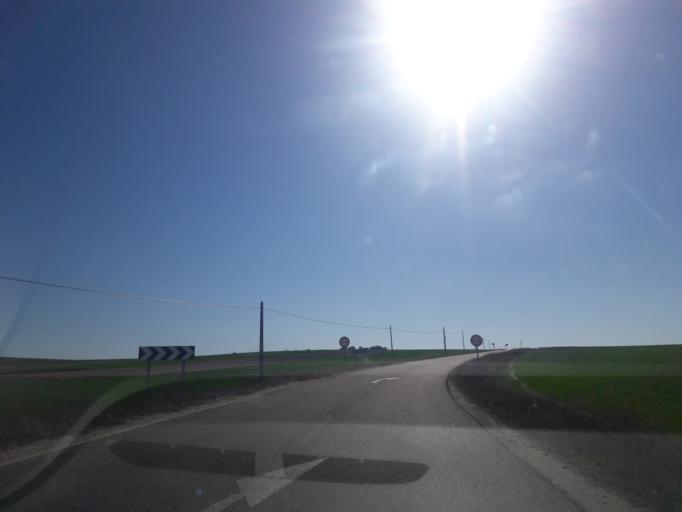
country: ES
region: Castille and Leon
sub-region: Provincia de Salamanca
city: Tordillos
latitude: 40.8486
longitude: -5.3188
